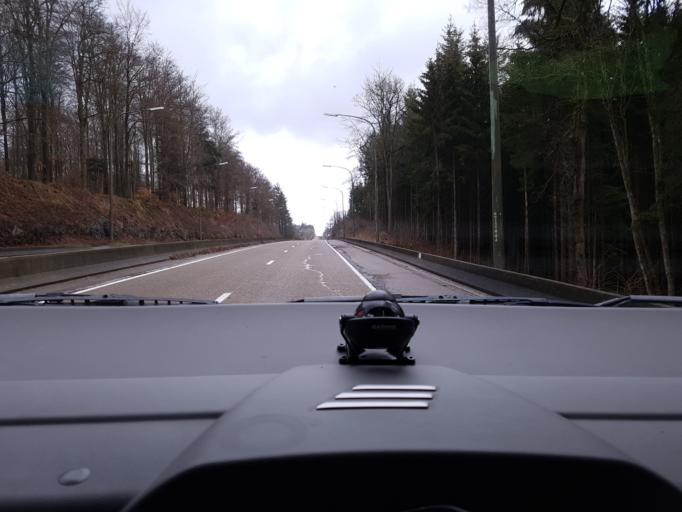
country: BE
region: Wallonia
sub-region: Province du Luxembourg
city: Tenneville
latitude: 50.0947
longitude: 5.4854
